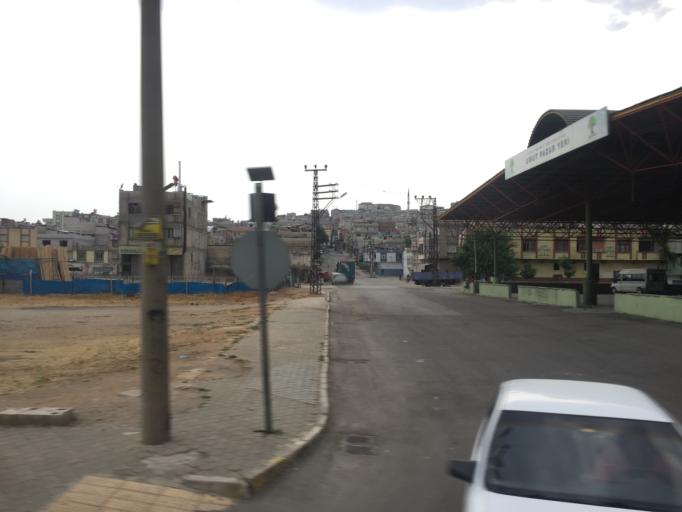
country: TR
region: Gaziantep
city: Gaziantep
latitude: 37.0692
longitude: 37.4138
